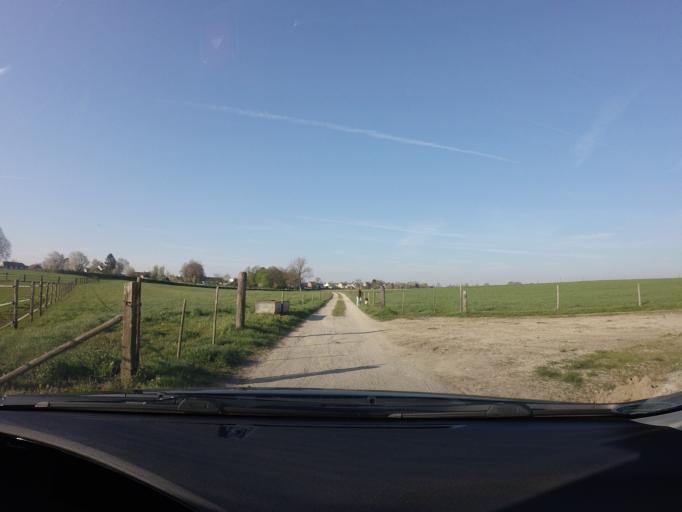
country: NL
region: Limburg
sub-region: Gemeente Beek
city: Beek
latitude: 50.9115
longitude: 5.8226
